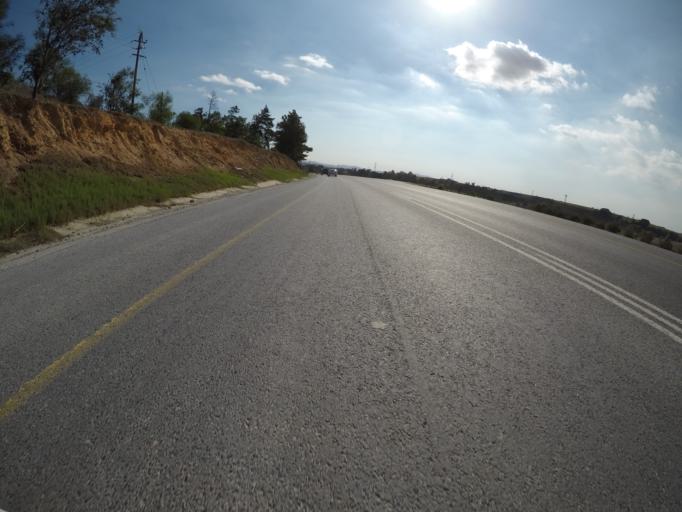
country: ZA
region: Western Cape
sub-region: City of Cape Town
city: Kraaifontein
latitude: -33.8773
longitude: 18.7722
